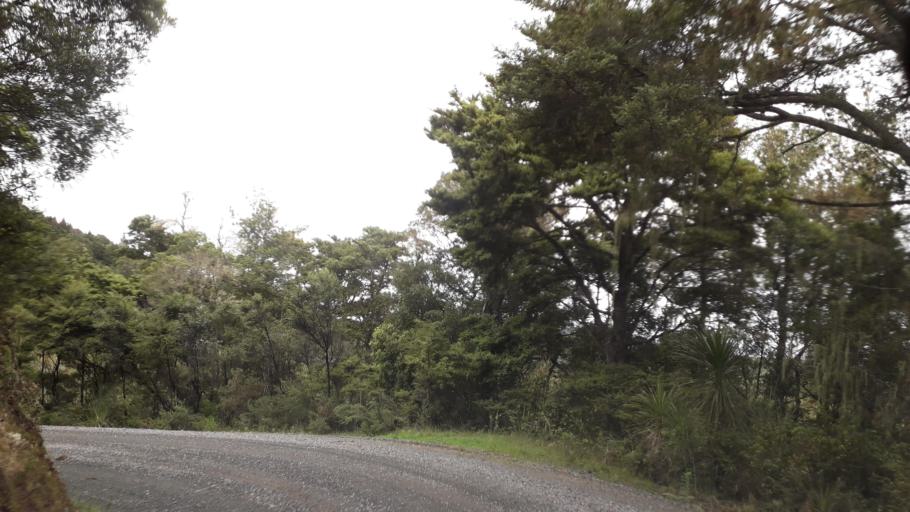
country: NZ
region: Northland
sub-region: Far North District
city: Waimate North
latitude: -35.3062
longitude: 173.5627
